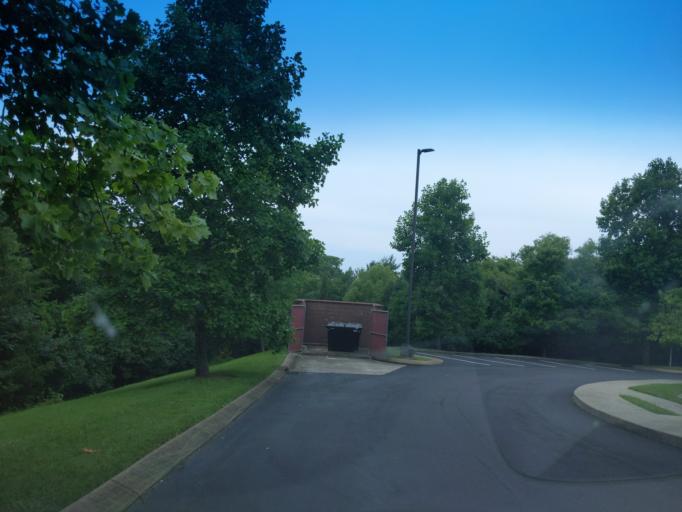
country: US
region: Tennessee
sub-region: Williamson County
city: Brentwood
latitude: 36.0305
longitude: -86.7784
